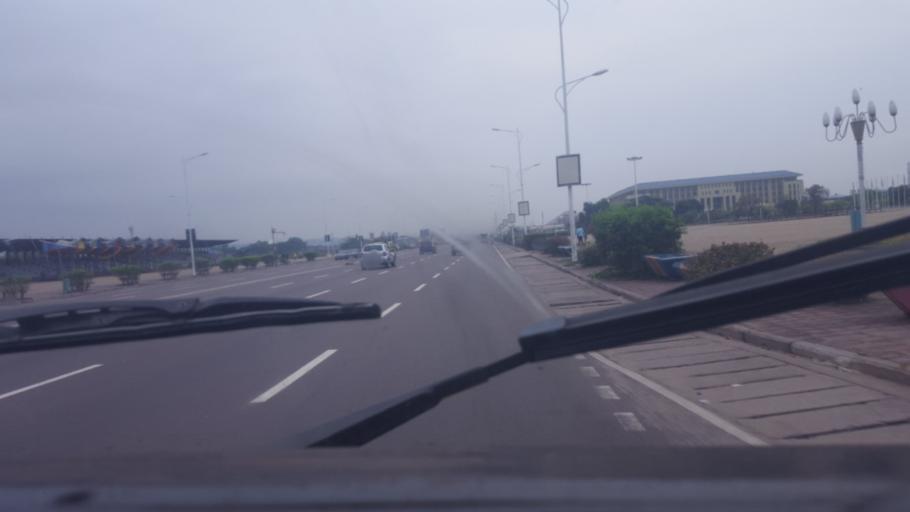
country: CD
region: Kinshasa
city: Kinshasa
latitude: -4.3343
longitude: 15.3049
